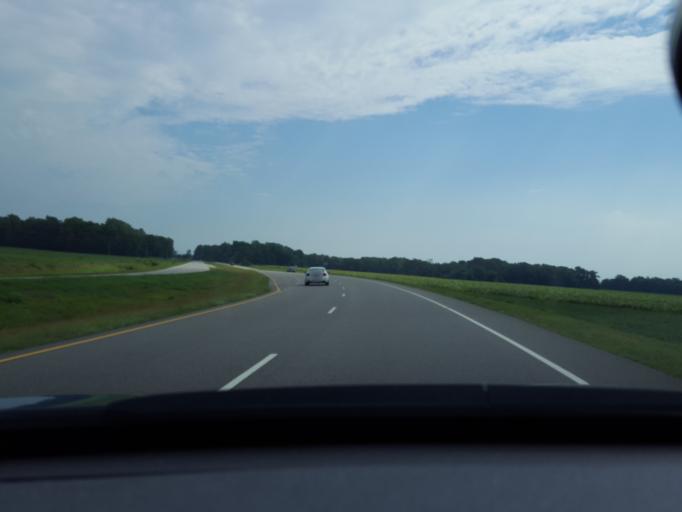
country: US
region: North Carolina
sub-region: Chowan County
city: Edenton
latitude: 36.0361
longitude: -76.7239
